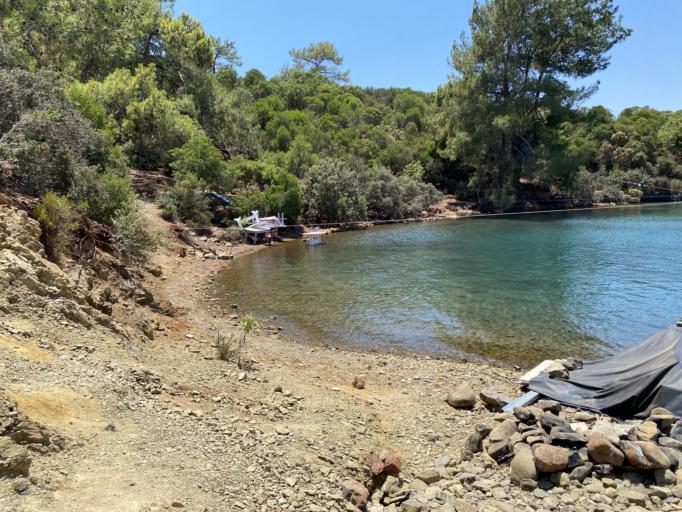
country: TR
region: Mugla
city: Goecek
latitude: 36.7080
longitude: 28.9349
